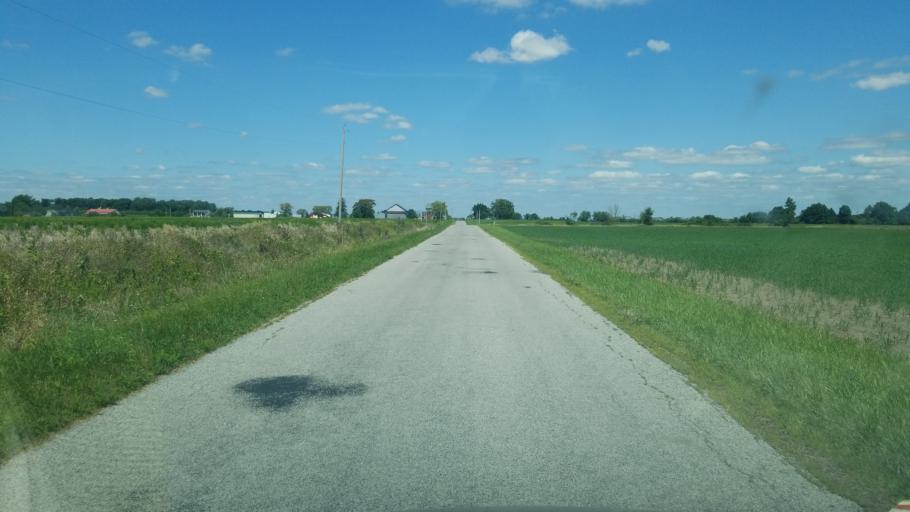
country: US
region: Ohio
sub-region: Fulton County
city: Delta
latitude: 41.6584
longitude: -84.0160
